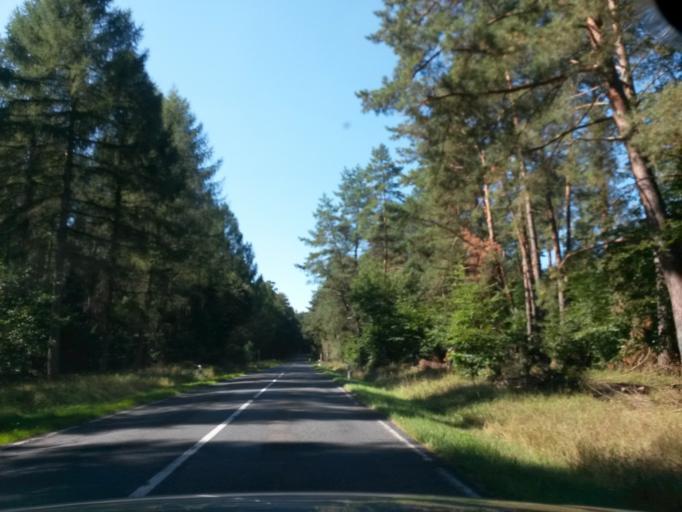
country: DE
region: Brandenburg
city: Lychen
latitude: 53.2429
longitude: 13.4401
